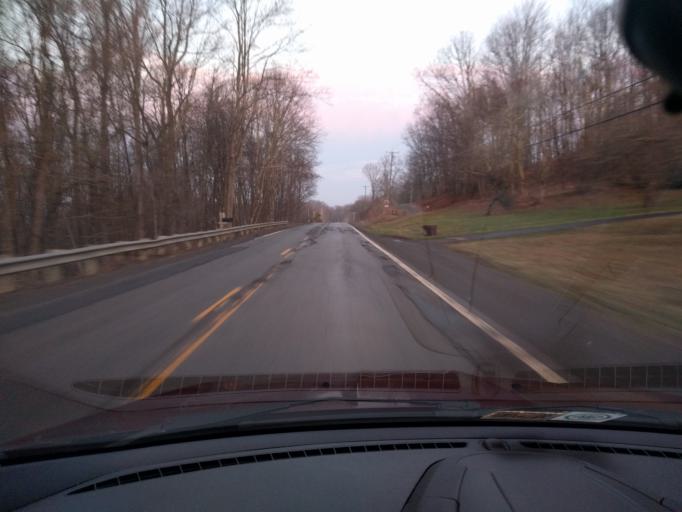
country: US
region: West Virginia
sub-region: Greenbrier County
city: Rainelle
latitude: 38.0124
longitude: -80.8940
